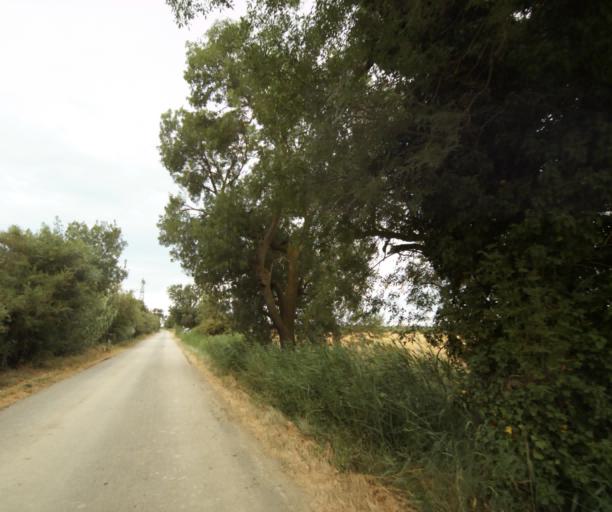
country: FR
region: Languedoc-Roussillon
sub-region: Departement de l'Herault
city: Saint-Just
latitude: 43.6133
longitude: 4.1429
